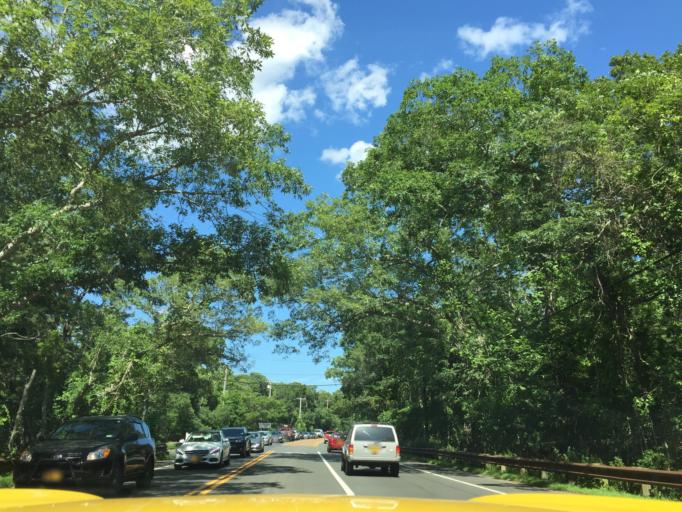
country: US
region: New York
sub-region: Suffolk County
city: East Hampton North
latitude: 40.9523
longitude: -72.2340
